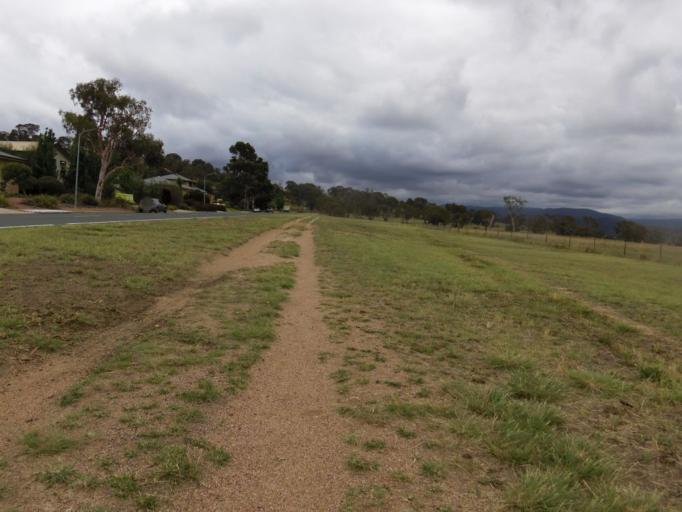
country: AU
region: Australian Capital Territory
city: Macquarie
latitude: -35.3476
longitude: 149.0261
